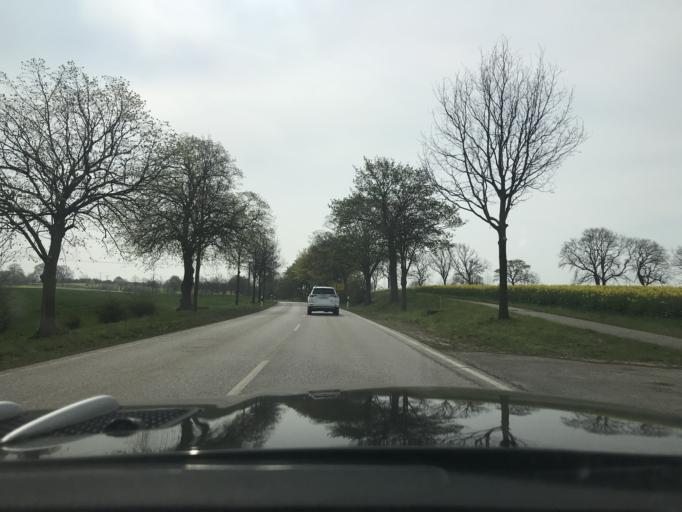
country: DE
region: Schleswig-Holstein
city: Heringsdorf
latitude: 54.2836
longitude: 11.0181
